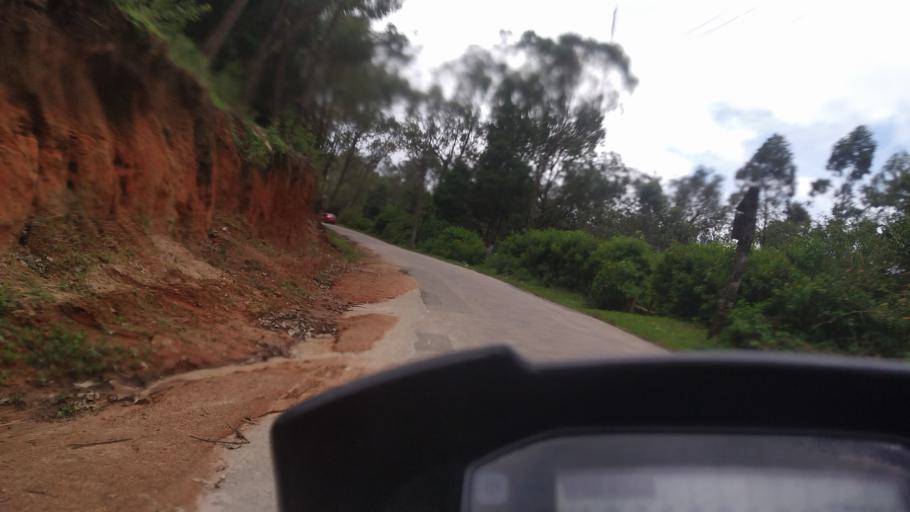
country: IN
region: Kerala
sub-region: Idukki
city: Munnar
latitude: 10.0651
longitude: 77.1031
